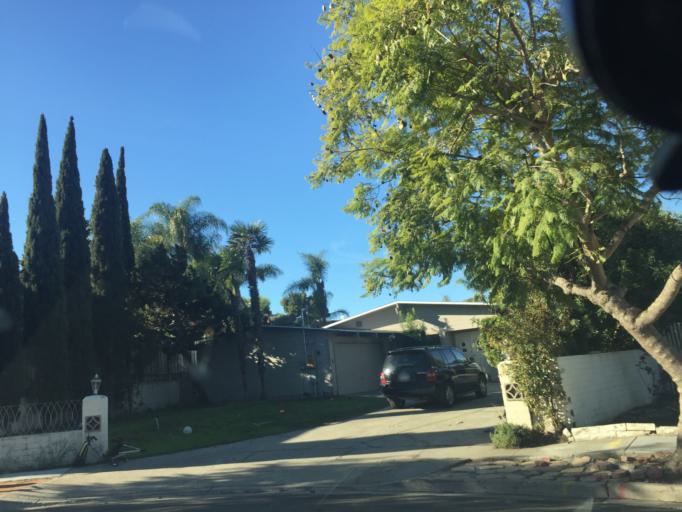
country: US
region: California
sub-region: San Diego County
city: La Mesa
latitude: 32.7790
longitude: -117.0852
